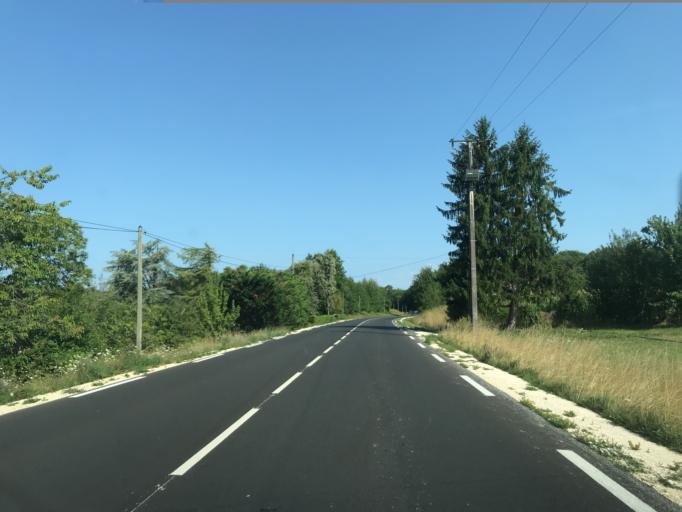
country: FR
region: Aquitaine
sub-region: Departement de la Dordogne
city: Montignac
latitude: 45.0168
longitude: 1.2366
